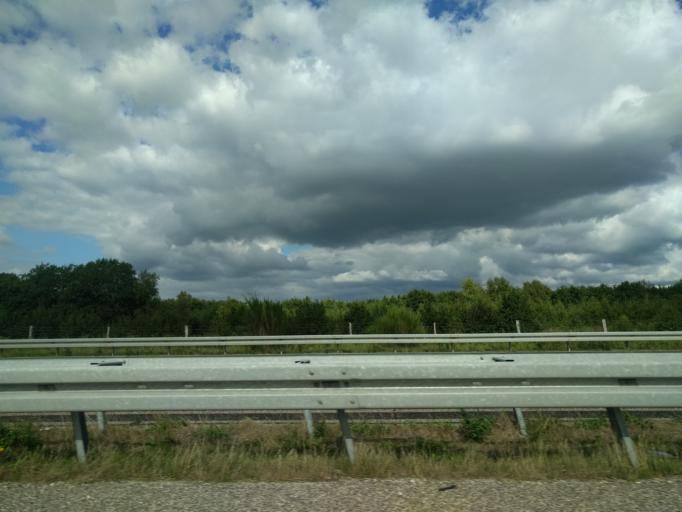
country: DK
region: South Denmark
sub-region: Vejle Kommune
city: Give
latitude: 55.8738
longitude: 9.2425
